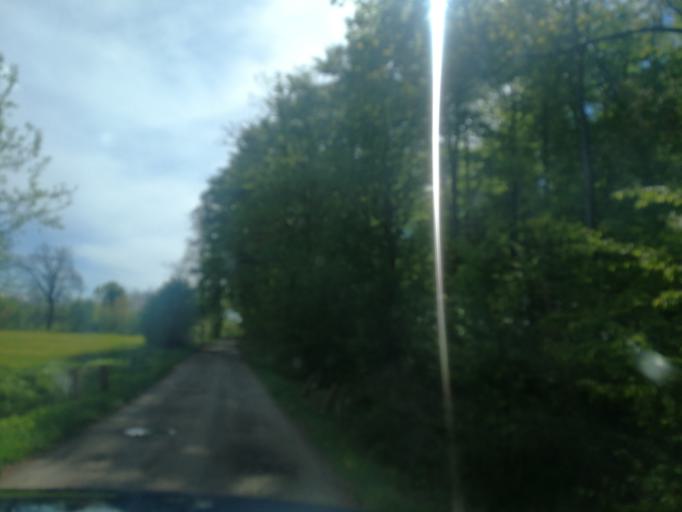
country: PL
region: Warmian-Masurian Voivodeship
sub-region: Powiat ilawski
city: Zalewo
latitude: 53.7601
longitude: 19.6810
